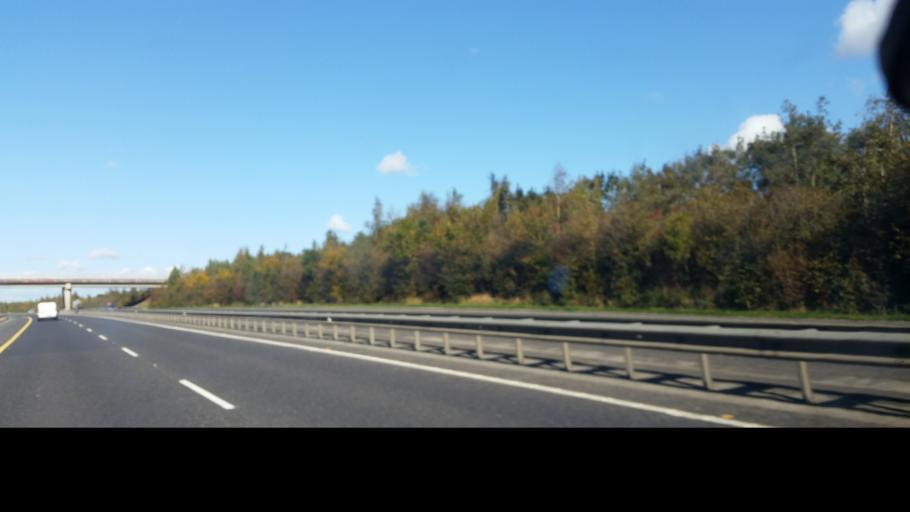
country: IE
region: Leinster
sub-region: An Mhi
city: Ashbourne
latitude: 53.4799
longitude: -6.3728
